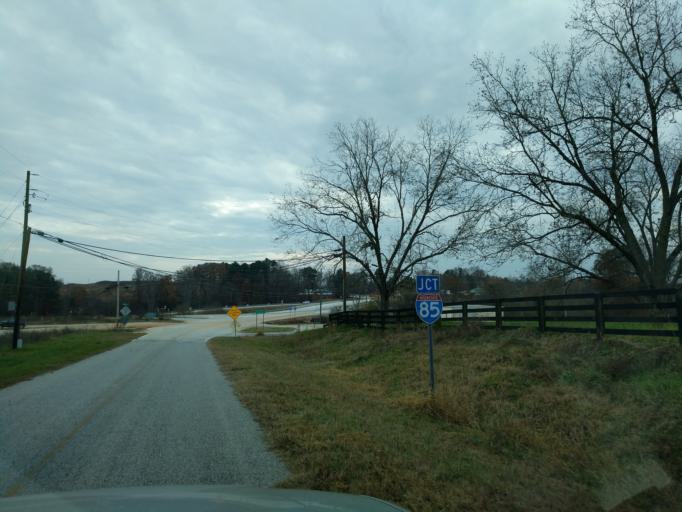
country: US
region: Georgia
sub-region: Franklin County
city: Gumlog
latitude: 34.4774
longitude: -83.0581
